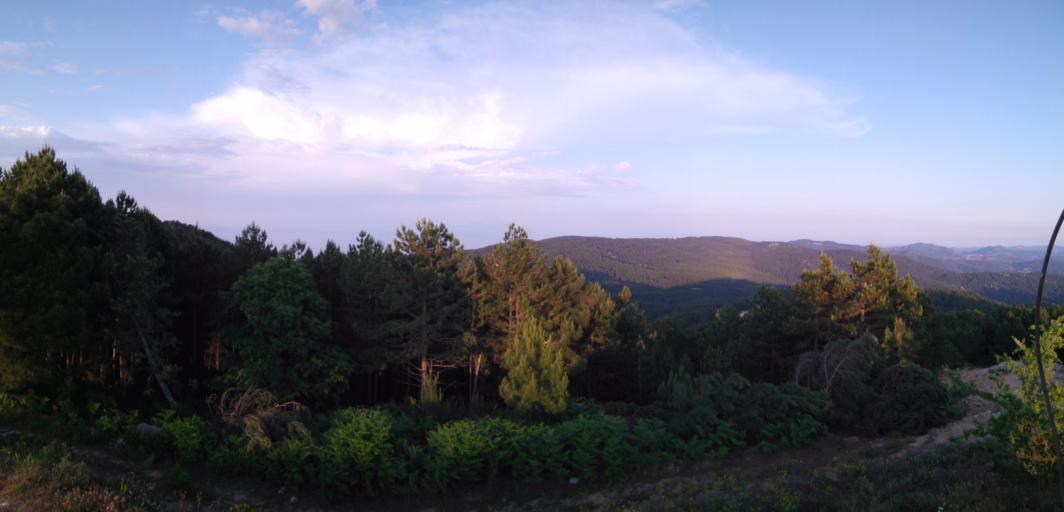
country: GR
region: Central Macedonia
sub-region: Nomos Chalkidikis
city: Neos Marmaras
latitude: 40.1243
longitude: 23.8536
